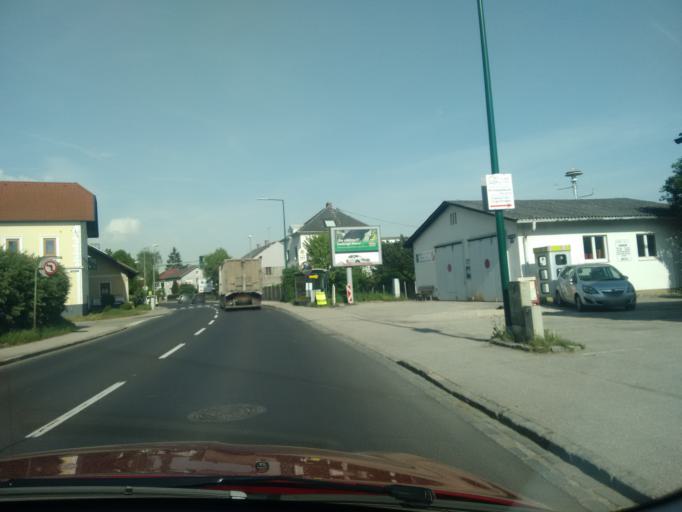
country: AT
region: Upper Austria
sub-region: Wels Stadt
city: Wels
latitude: 48.1674
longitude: 14.0470
